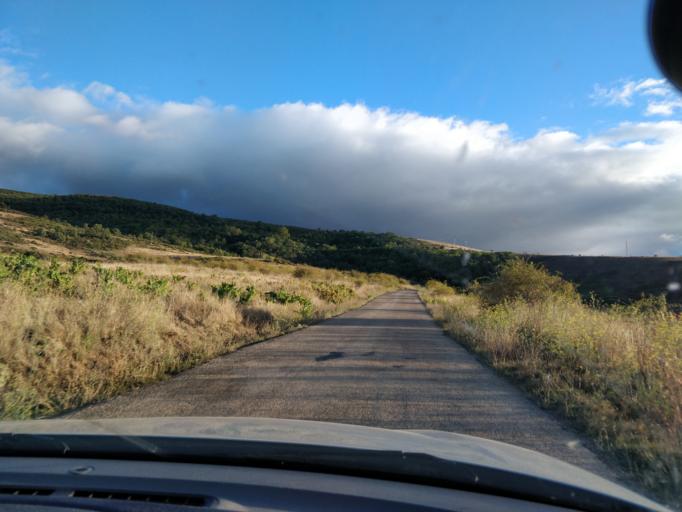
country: ES
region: Castille and Leon
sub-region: Provincia de Leon
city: Borrenes
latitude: 42.4883
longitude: -6.7017
